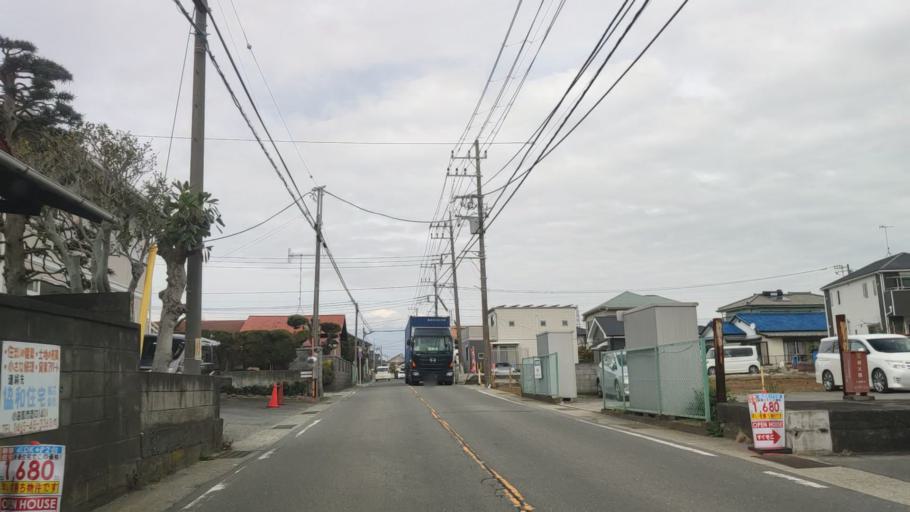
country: JP
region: Kanagawa
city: Ninomiya
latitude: 35.2937
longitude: 139.2337
